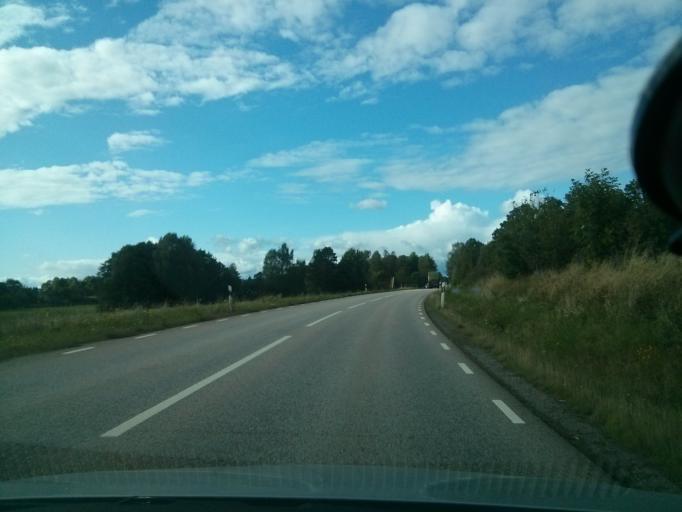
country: SE
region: Blekinge
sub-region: Ronneby Kommun
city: Brakne-Hoby
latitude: 56.3001
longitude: 15.1937
